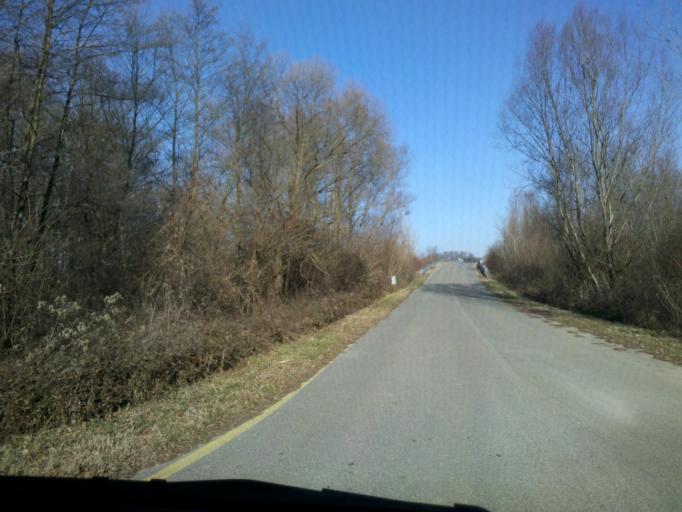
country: HR
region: Medimurska
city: Gorican
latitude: 46.4056
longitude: 16.6730
